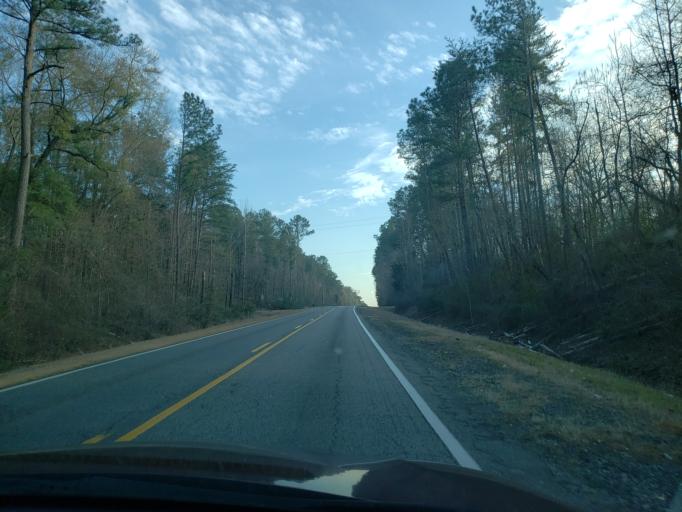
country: US
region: Alabama
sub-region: Hale County
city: Greensboro
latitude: 32.7482
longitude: -87.5851
